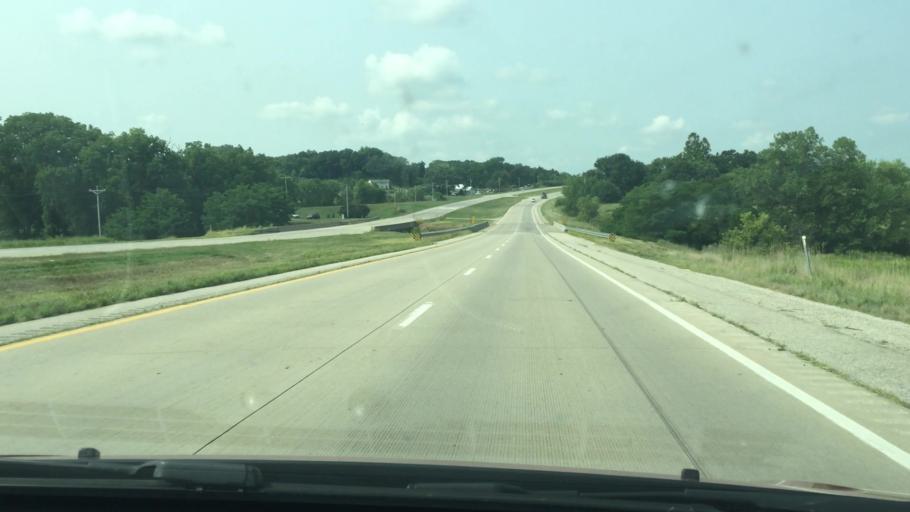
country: US
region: Iowa
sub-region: Cedar County
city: Durant
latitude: 41.5043
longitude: -90.9343
